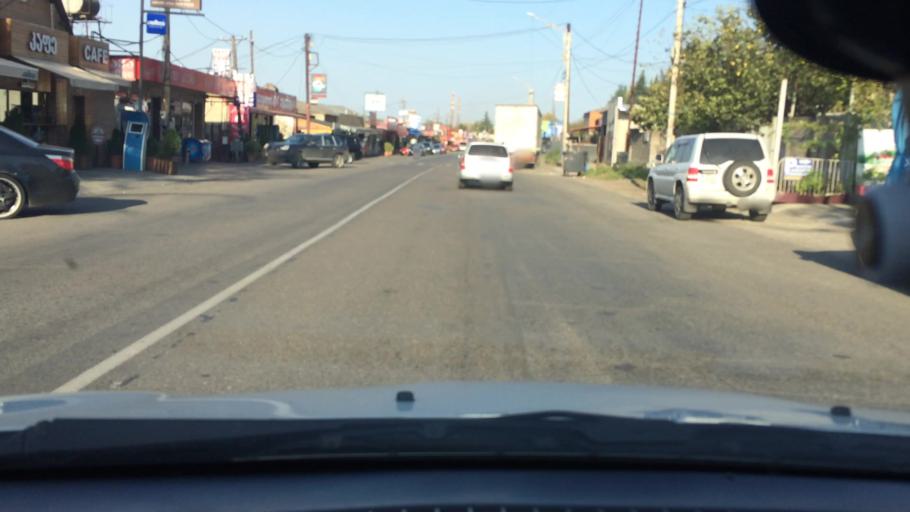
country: GE
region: Imereti
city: Zestap'oni
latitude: 42.1119
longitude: 43.0393
